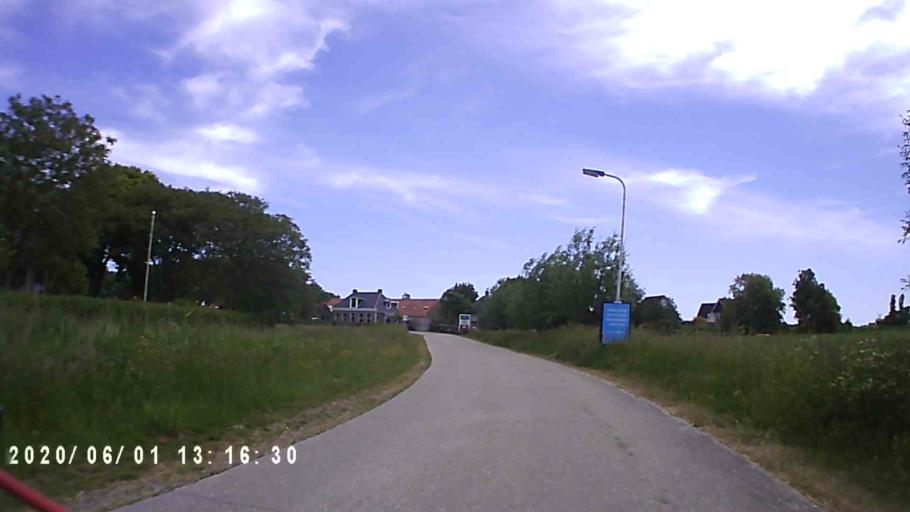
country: NL
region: Friesland
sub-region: Gemeente Littenseradiel
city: Wommels
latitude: 53.1194
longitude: 5.5669
